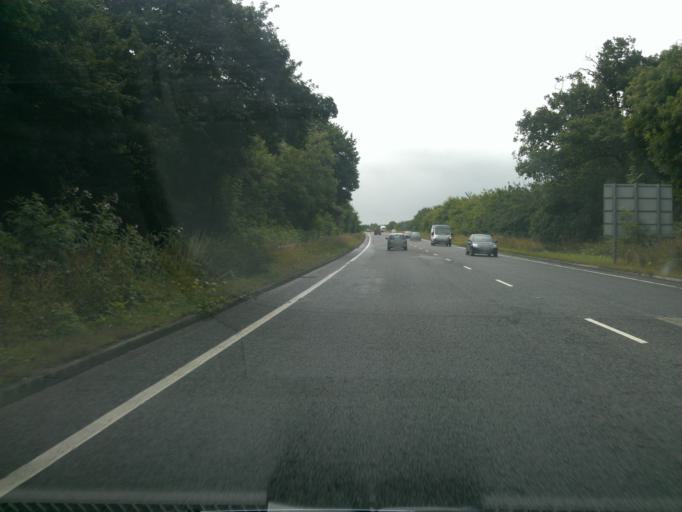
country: GB
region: England
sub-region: Essex
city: Little Clacton
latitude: 51.8186
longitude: 1.1373
